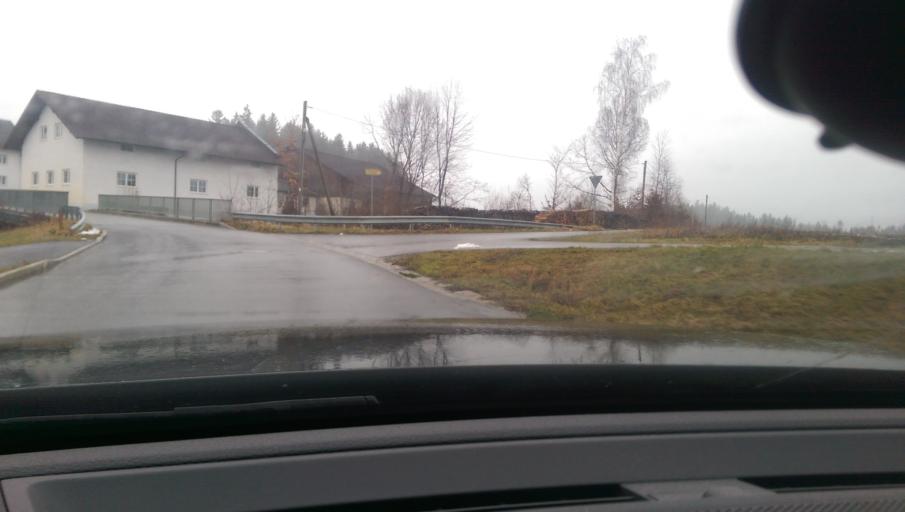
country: DE
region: Bavaria
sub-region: Lower Bavaria
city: Tiefenbach
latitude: 48.6200
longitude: 13.4232
